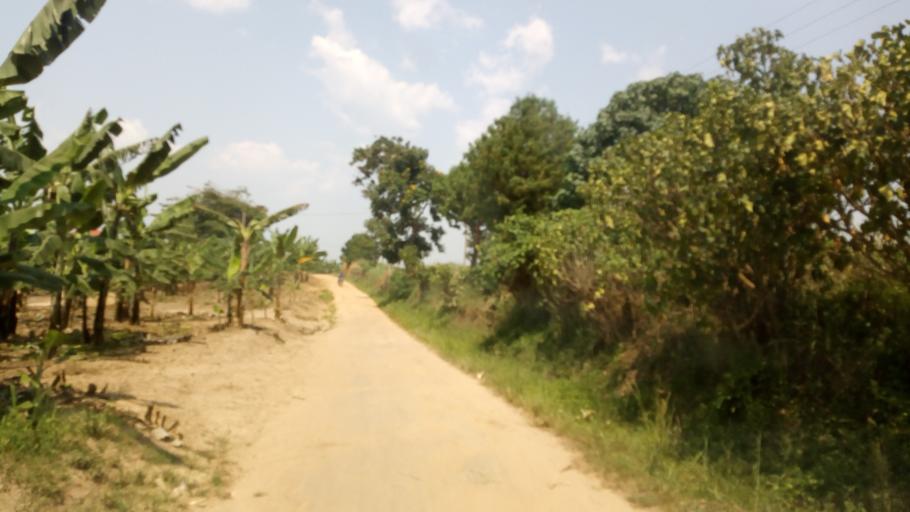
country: UG
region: Western Region
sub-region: Kanungu District
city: Ntungamo
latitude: -0.8028
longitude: 29.6511
